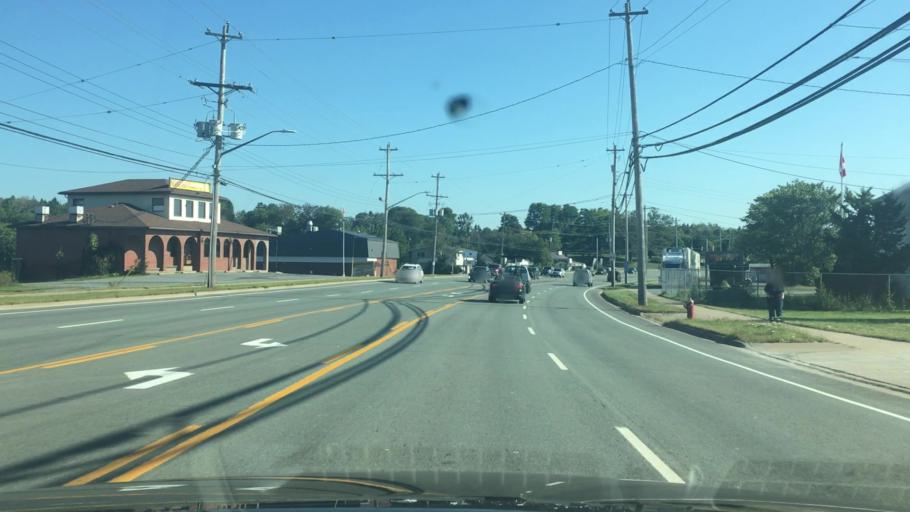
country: CA
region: Nova Scotia
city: Cole Harbour
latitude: 44.6964
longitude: -63.4958
